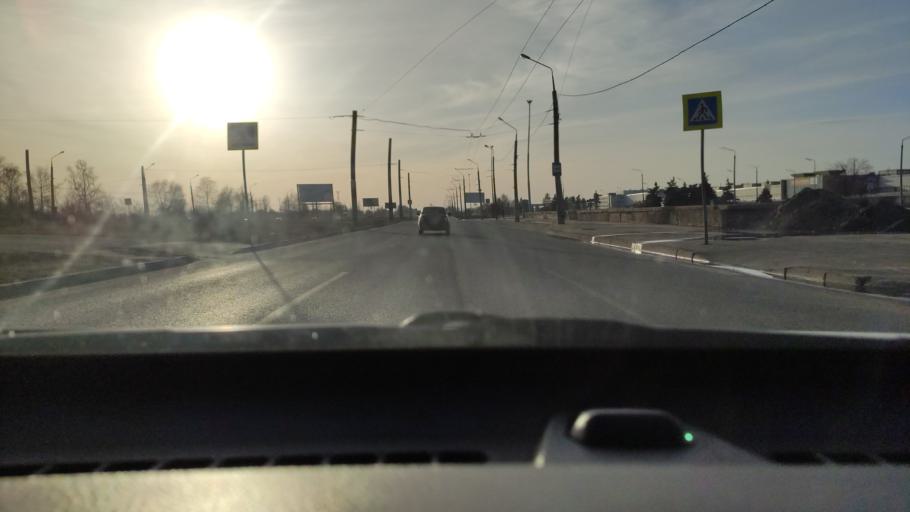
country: RU
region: Samara
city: Tol'yatti
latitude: 53.5590
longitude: 49.2439
